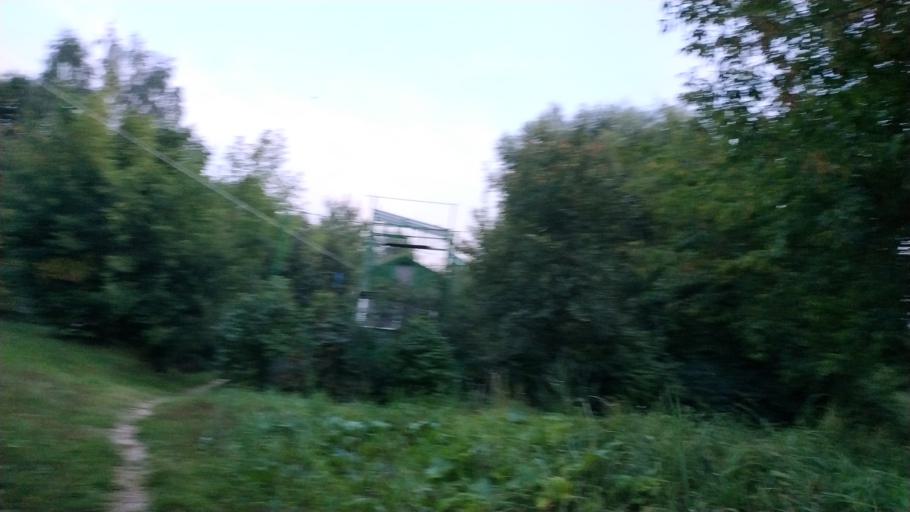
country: RU
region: Moscow
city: Solntsevo
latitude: 55.6383
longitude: 37.3756
